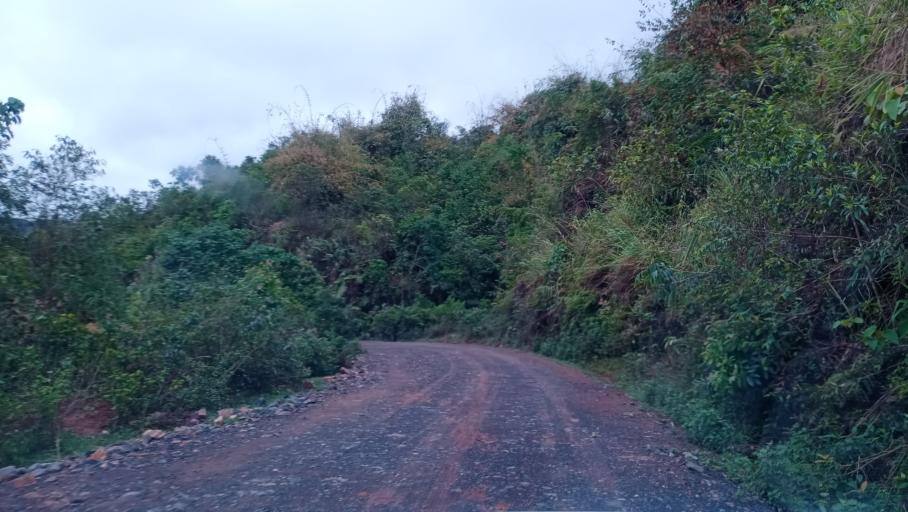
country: LA
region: Phongsali
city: Phongsali
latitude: 21.3401
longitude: 102.0832
